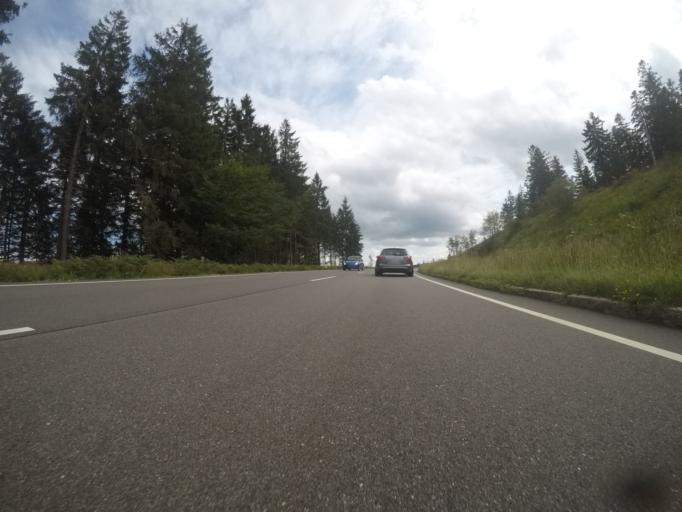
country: DE
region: Baden-Wuerttemberg
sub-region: Freiburg Region
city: Seebach
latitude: 48.5474
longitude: 8.2178
